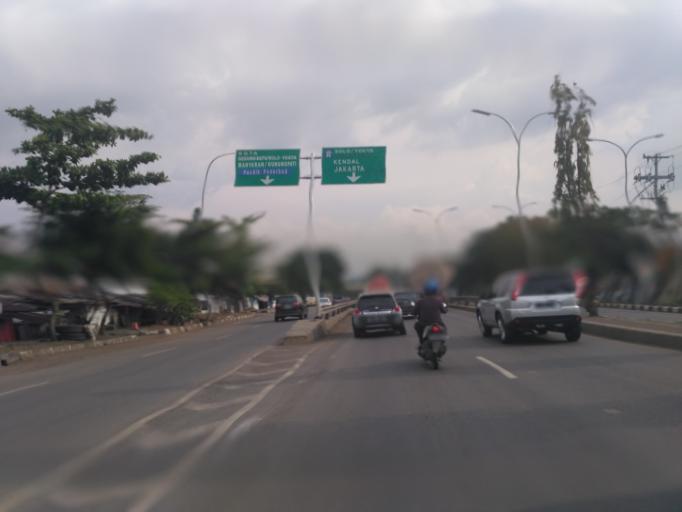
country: ID
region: Central Java
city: Semarang
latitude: -6.9821
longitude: 110.3863
